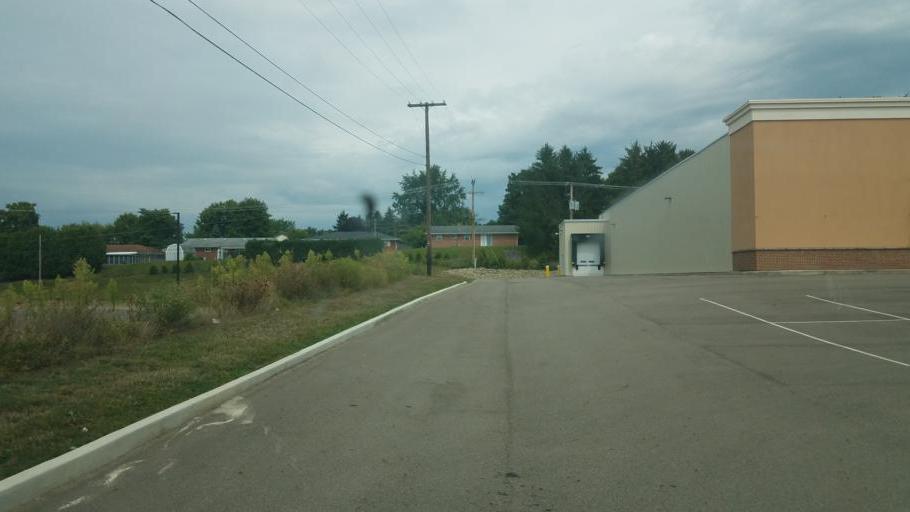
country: US
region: Ohio
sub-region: Knox County
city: Mount Vernon
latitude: 40.4013
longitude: -82.4549
